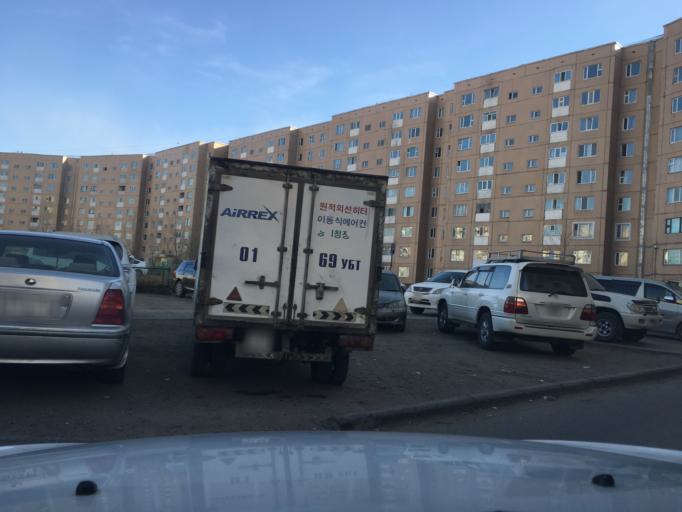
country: MN
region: Ulaanbaatar
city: Ulaanbaatar
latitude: 47.9134
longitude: 106.8469
